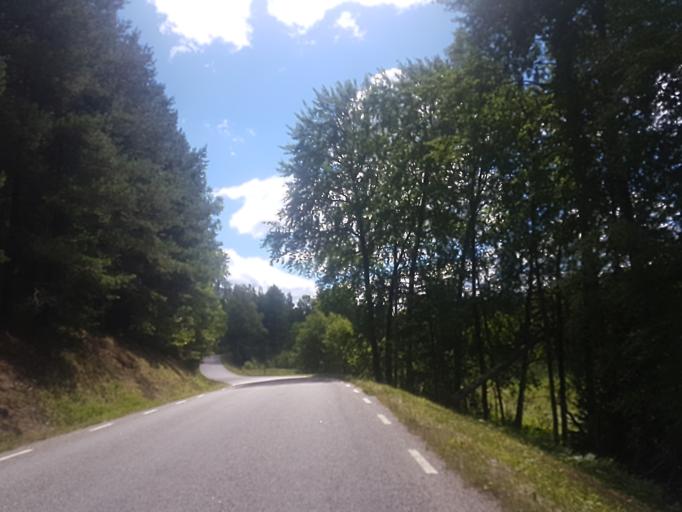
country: SE
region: Soedermanland
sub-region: Gnesta Kommun
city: Gnesta
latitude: 59.0388
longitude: 17.3468
